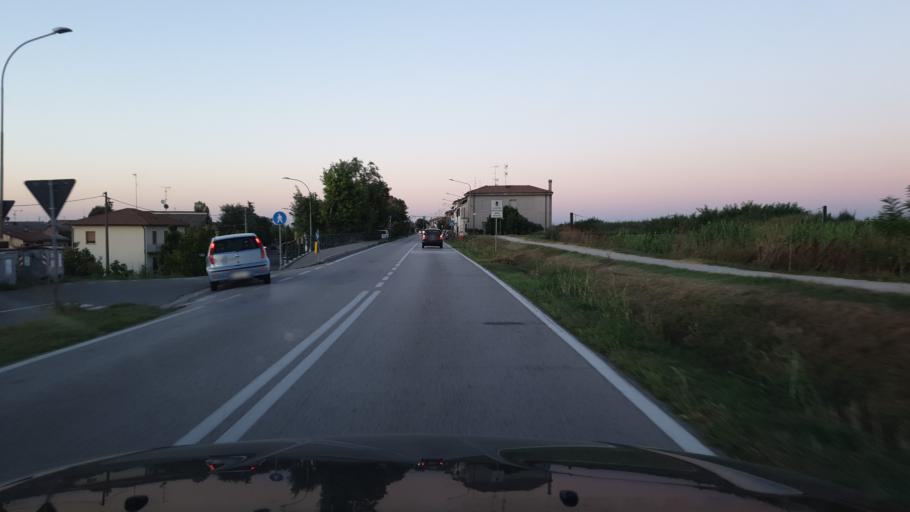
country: IT
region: Emilia-Romagna
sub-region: Provincia di Bologna
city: Ca De Fabbri
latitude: 44.6263
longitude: 11.4599
